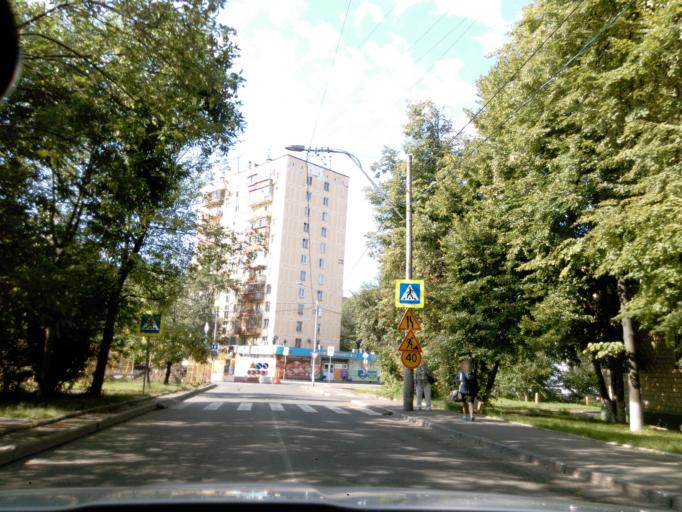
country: RU
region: Moskovskaya
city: Koptevo
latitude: 55.8285
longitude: 37.5249
